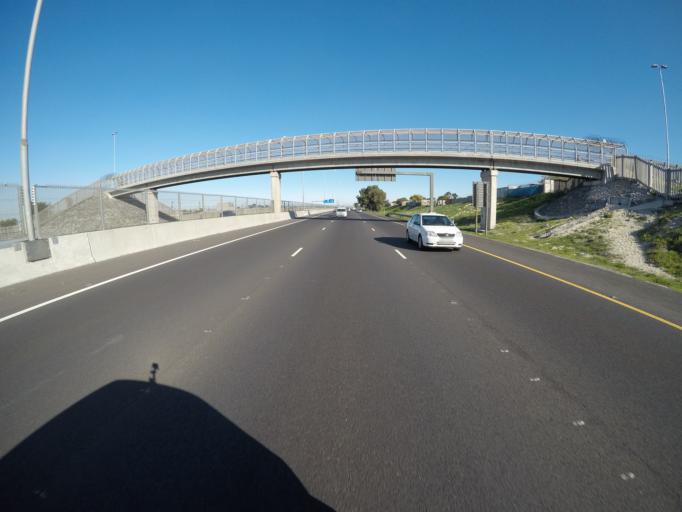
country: ZA
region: Western Cape
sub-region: City of Cape Town
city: Kraaifontein
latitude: -33.9677
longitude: 18.6546
